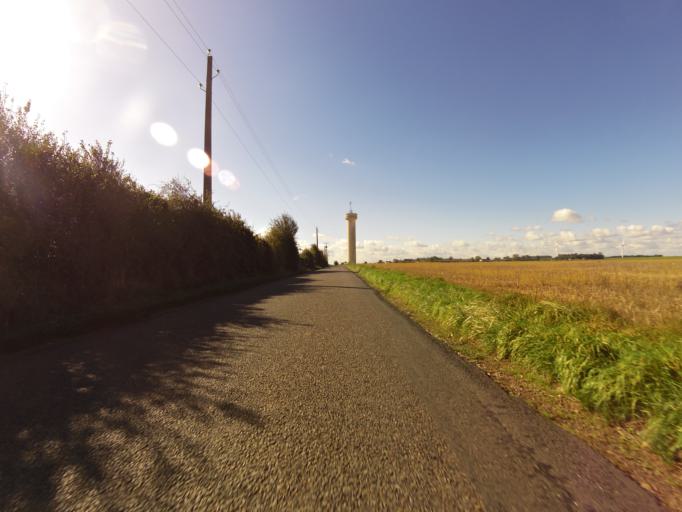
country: FR
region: Lower Normandy
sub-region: Departement du Calvados
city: Canon
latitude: 49.0527
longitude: -0.1210
